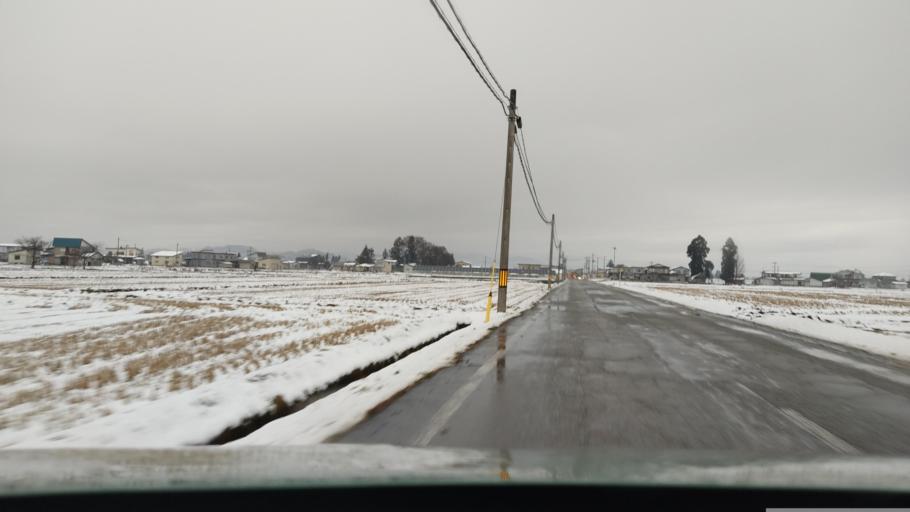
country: JP
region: Akita
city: Omagari
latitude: 39.4682
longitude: 140.5282
